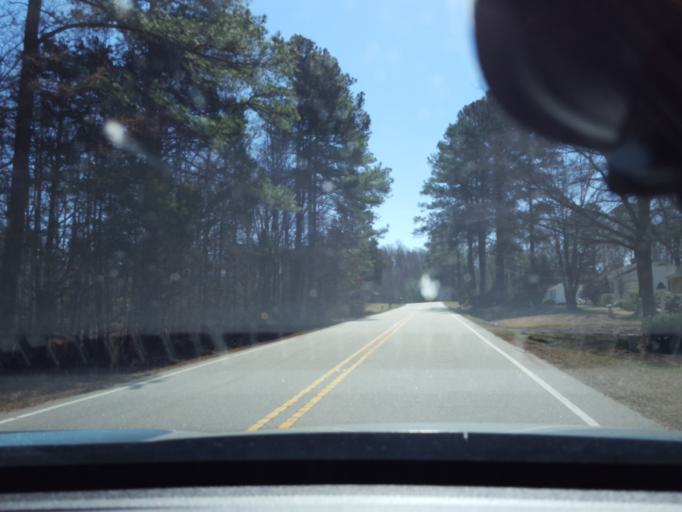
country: US
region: North Carolina
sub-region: Halifax County
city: South Rosemary
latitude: 36.4504
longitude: -77.9192
